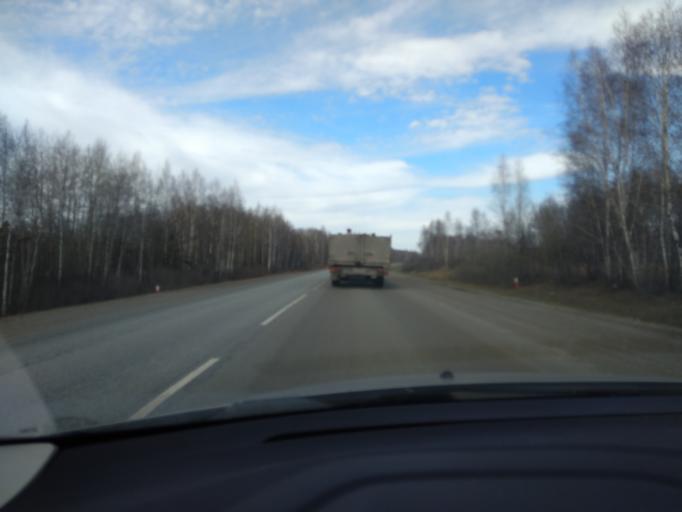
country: RU
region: Sverdlovsk
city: Pyshma
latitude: 56.9705
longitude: 63.2298
